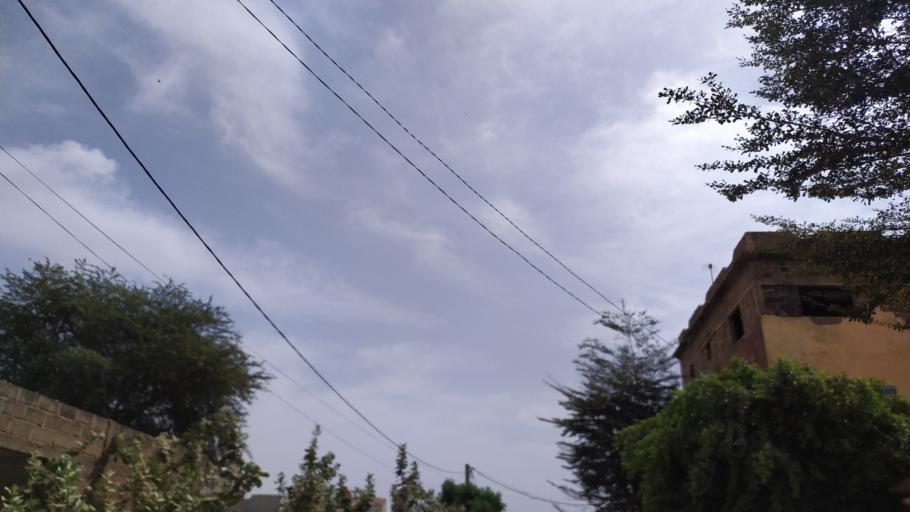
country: ML
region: Kayes
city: Kayes
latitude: 14.4560
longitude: -11.4646
